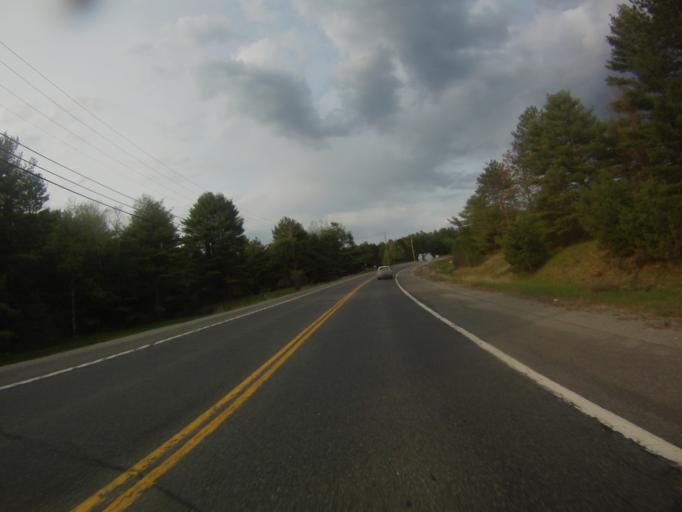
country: US
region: New York
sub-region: Warren County
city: Warrensburg
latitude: 43.6661
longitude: -73.7834
